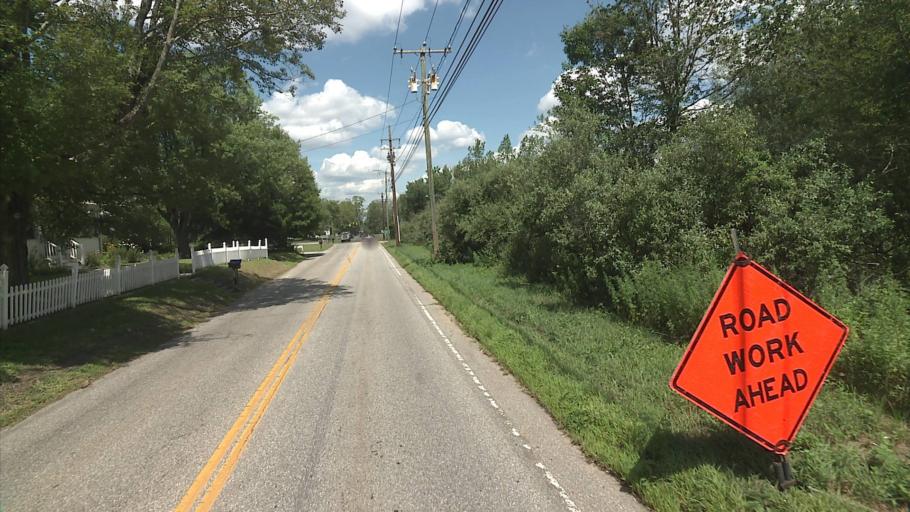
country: US
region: Connecticut
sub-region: Windham County
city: Windham
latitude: 41.7465
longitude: -72.1559
